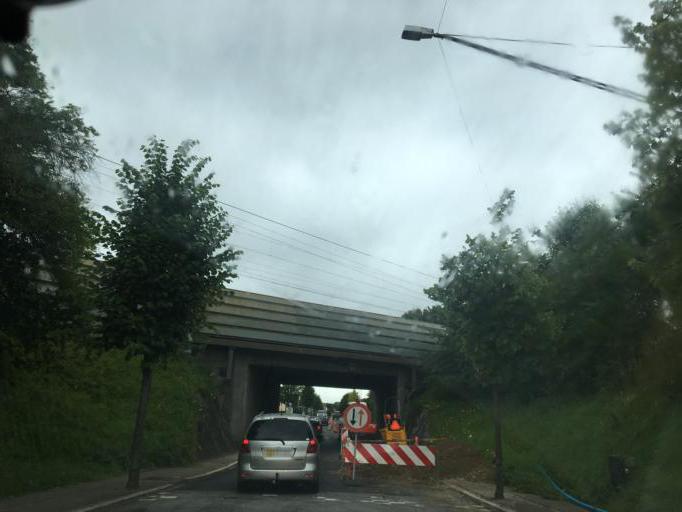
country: DK
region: South Denmark
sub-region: Middelfart Kommune
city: Middelfart
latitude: 55.4953
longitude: 9.7516
